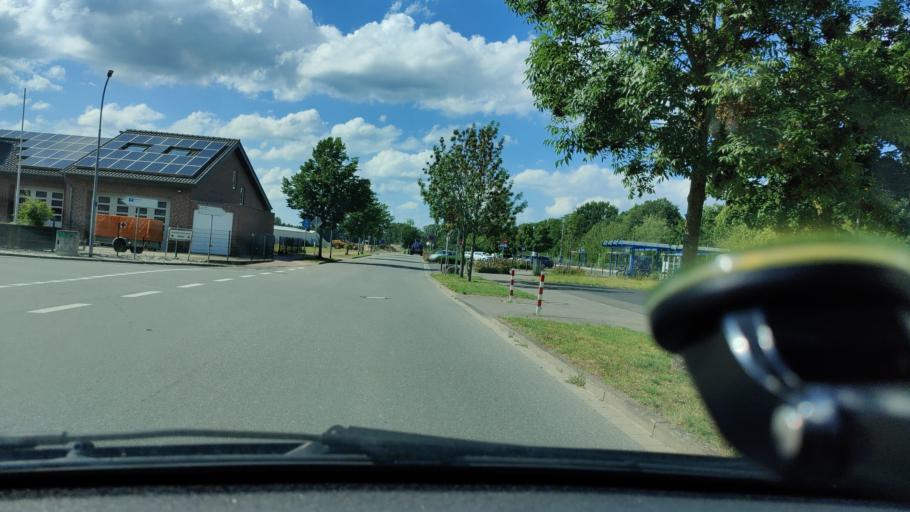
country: DE
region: North Rhine-Westphalia
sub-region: Regierungsbezirk Dusseldorf
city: Alpen
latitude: 51.5826
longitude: 6.5182
